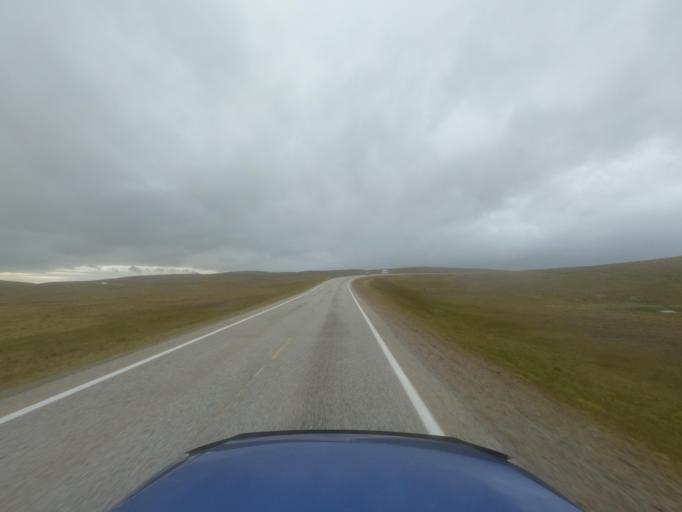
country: NO
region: Finnmark Fylke
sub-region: Nordkapp
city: Honningsvag
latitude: 71.0360
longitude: 25.8099
